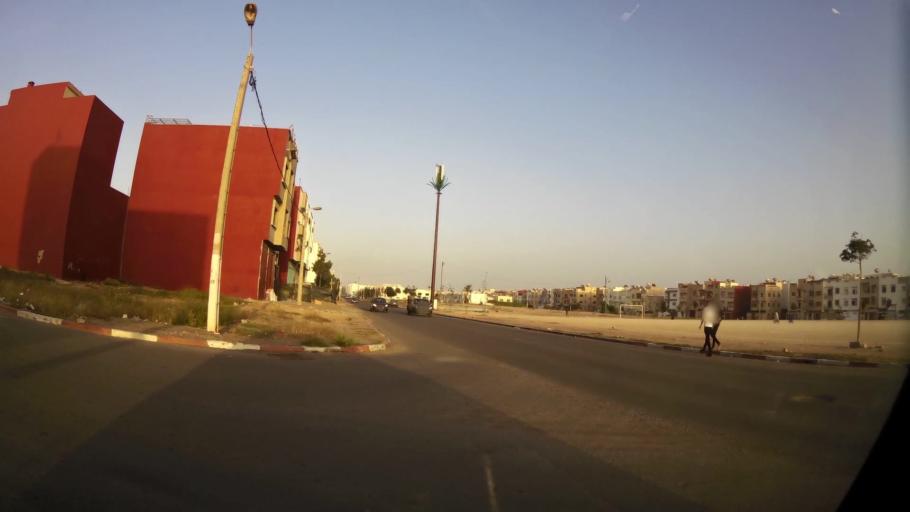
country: MA
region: Oued ed Dahab-Lagouira
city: Dakhla
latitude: 30.3956
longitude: -9.5619
